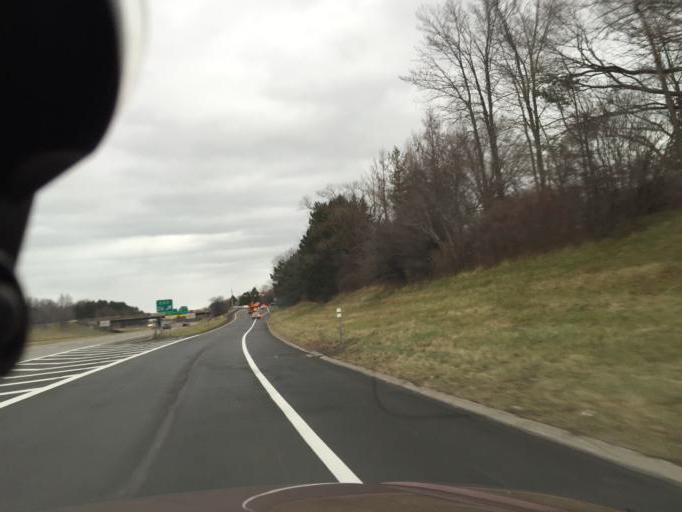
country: US
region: New York
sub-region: Monroe County
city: Greece
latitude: 43.2503
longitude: -77.6679
